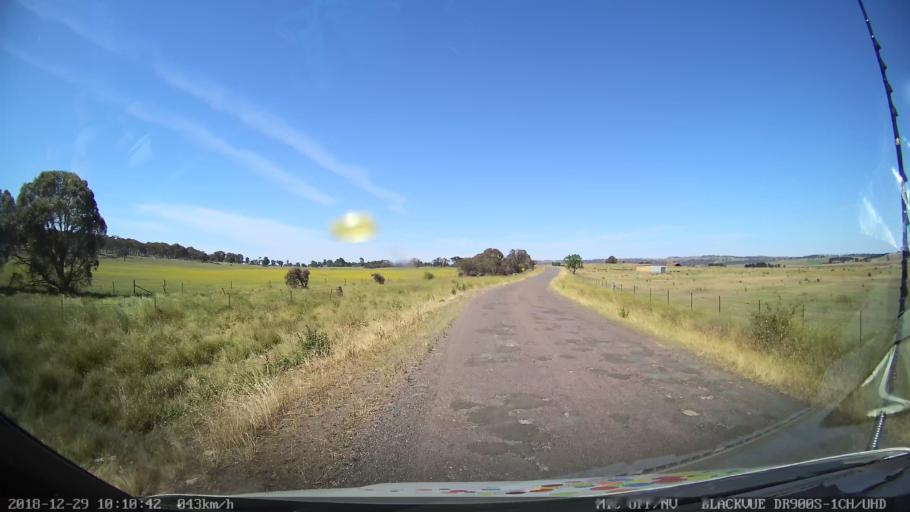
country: AU
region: New South Wales
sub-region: Yass Valley
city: Gundaroo
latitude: -34.8780
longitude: 149.4557
